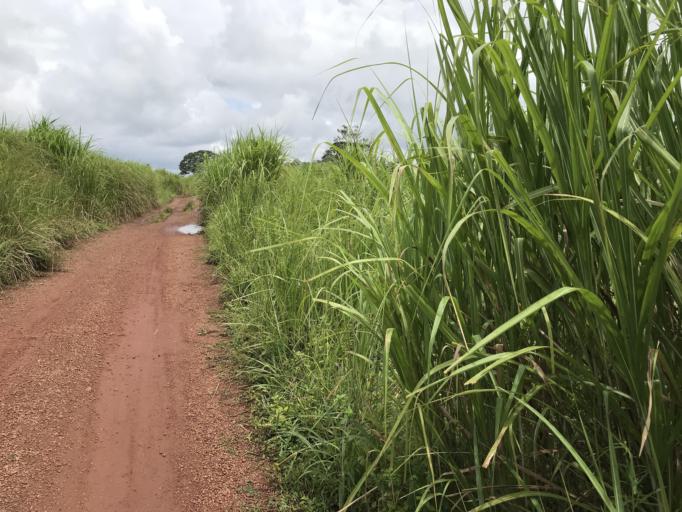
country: SL
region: Eastern Province
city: Buedu
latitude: 8.4700
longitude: -10.3255
